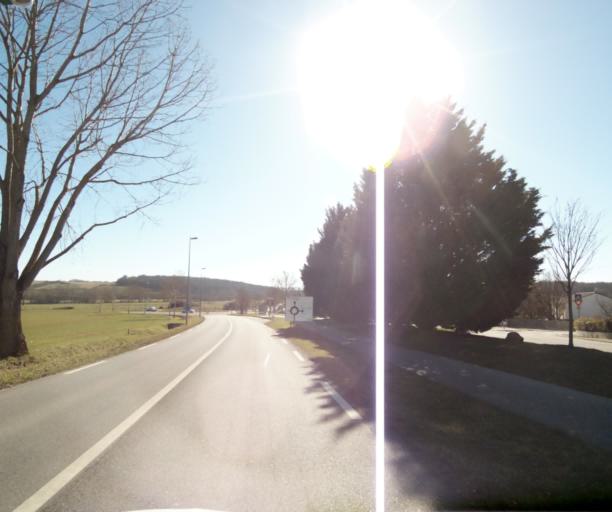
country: FR
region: Lorraine
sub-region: Departement de Meurthe-et-Moselle
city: Heillecourt
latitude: 48.6446
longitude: 6.2100
